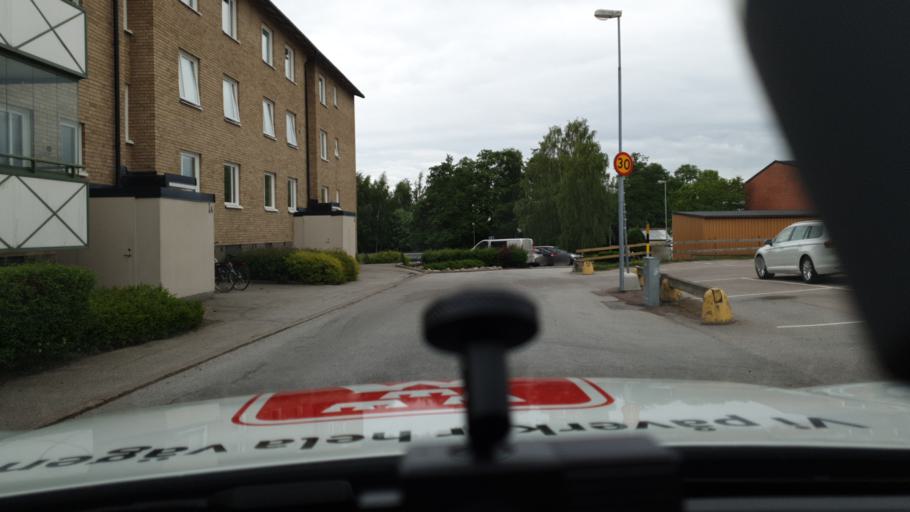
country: SE
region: Vaestra Goetaland
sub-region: Tibro Kommun
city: Tibro
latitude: 58.4219
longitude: 14.1674
